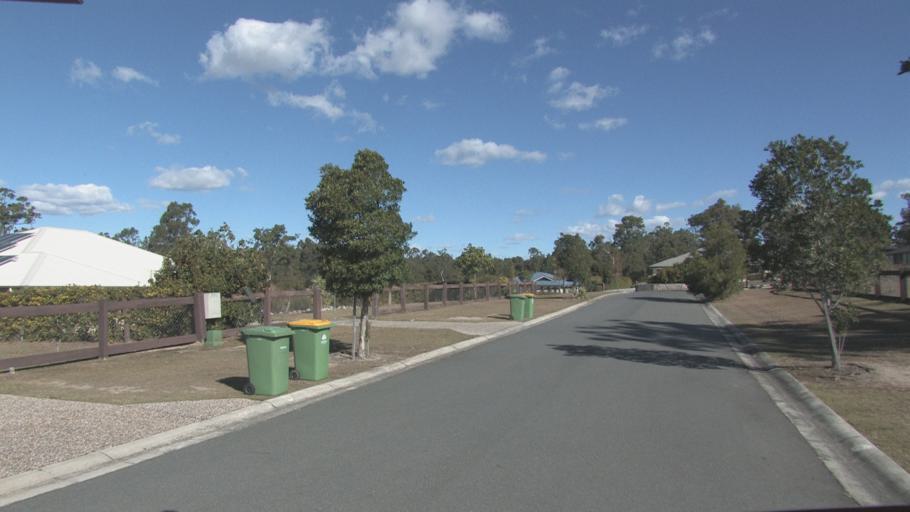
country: AU
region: Queensland
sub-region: Ipswich
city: Springfield Lakes
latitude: -27.7305
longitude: 152.9170
